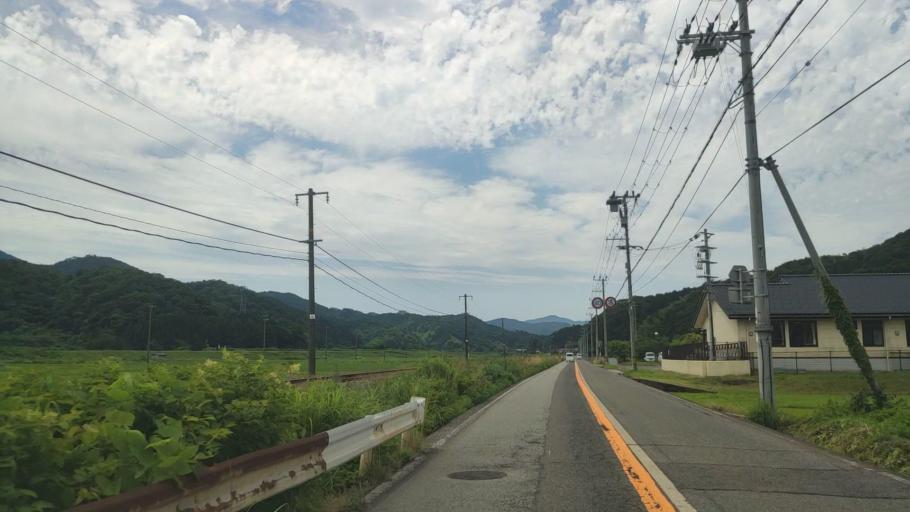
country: JP
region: Hyogo
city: Toyooka
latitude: 35.6410
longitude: 134.7580
